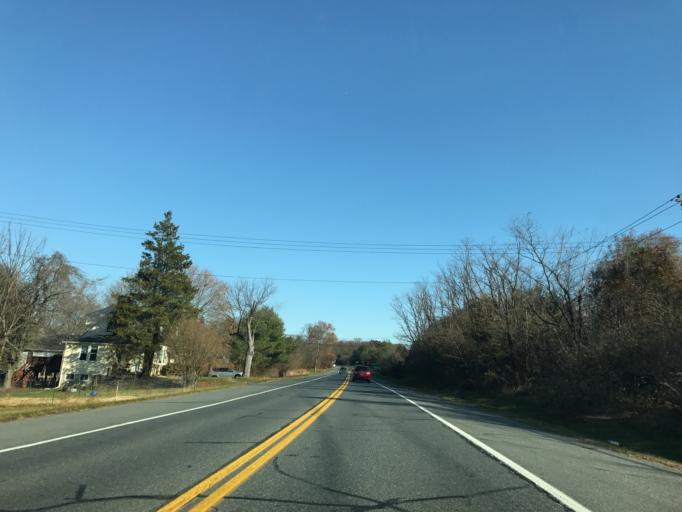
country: US
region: Maryland
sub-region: Howard County
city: Ellicott City
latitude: 39.2277
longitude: -76.8014
